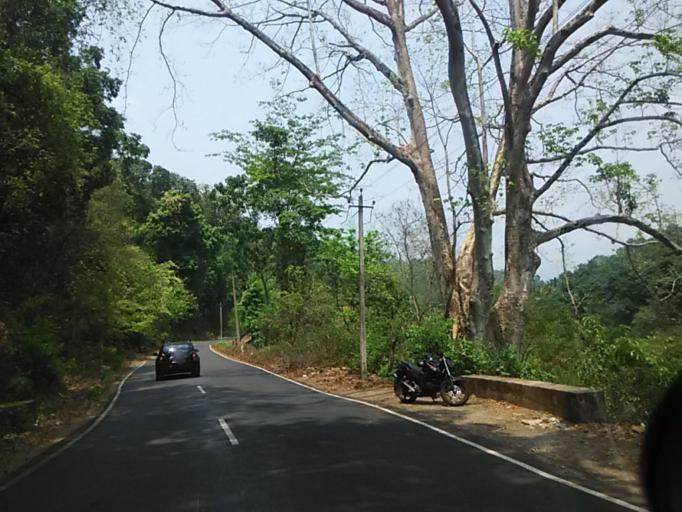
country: IN
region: Karnataka
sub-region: Kodagu
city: Virarajendrapet
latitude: 12.0713
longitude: 75.7202
